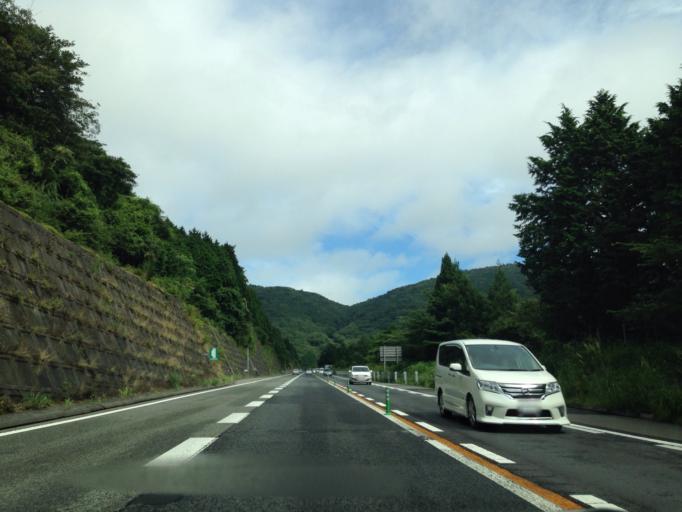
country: JP
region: Shizuoka
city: Gotemba
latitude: 35.3732
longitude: 138.8488
